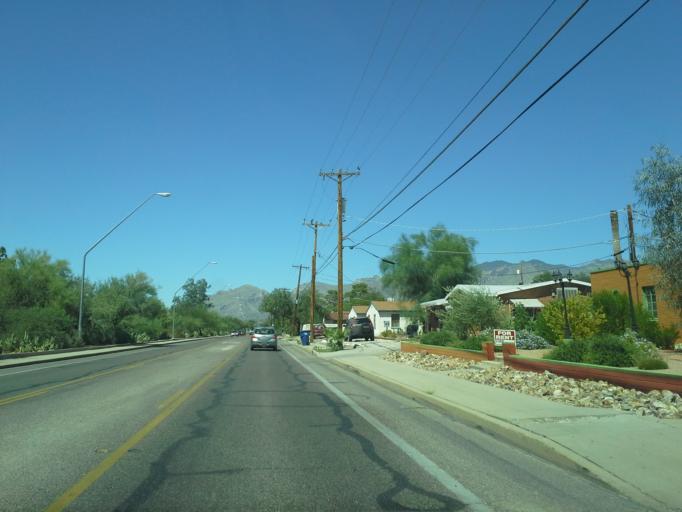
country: US
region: Arizona
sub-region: Pima County
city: Tucson
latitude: 32.2456
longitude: -110.9353
